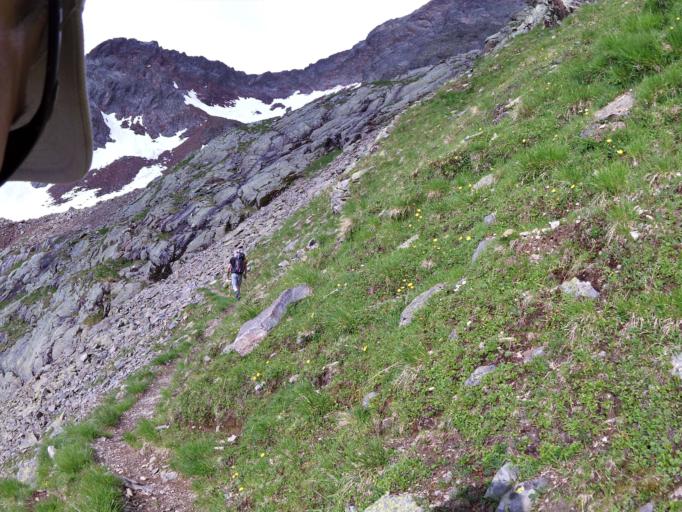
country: AT
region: Tyrol
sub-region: Politischer Bezirk Innsbruck Land
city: Gschnitz
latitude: 47.0404
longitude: 11.3035
